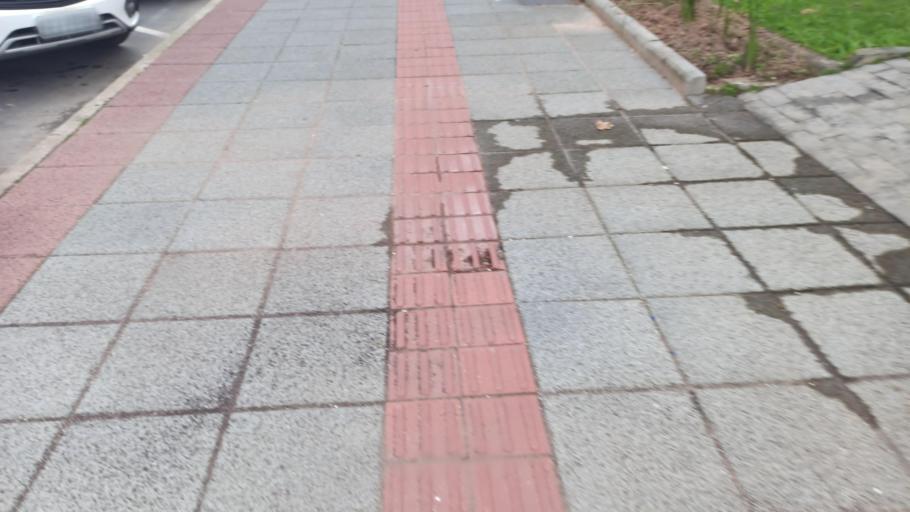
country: BR
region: Santa Catarina
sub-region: Joinville
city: Joinville
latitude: -26.3705
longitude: -48.7226
